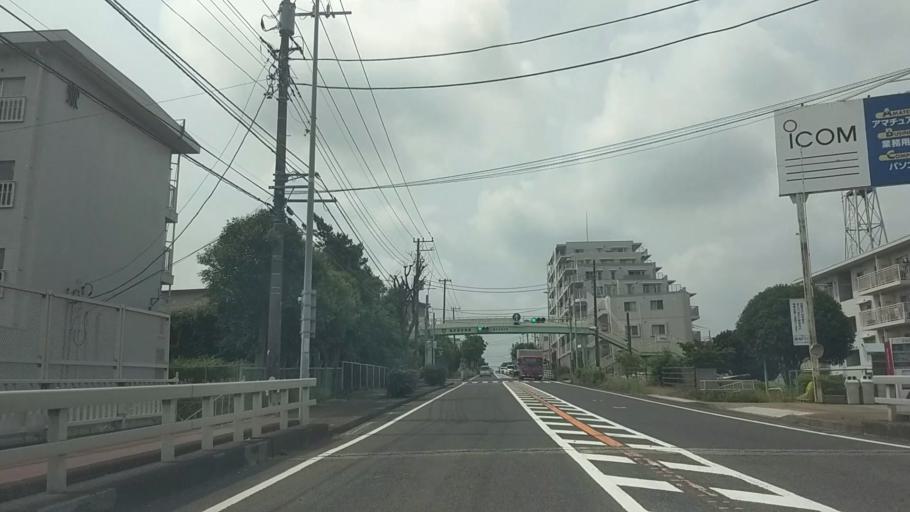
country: JP
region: Kanagawa
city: Fujisawa
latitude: 35.3682
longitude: 139.4790
